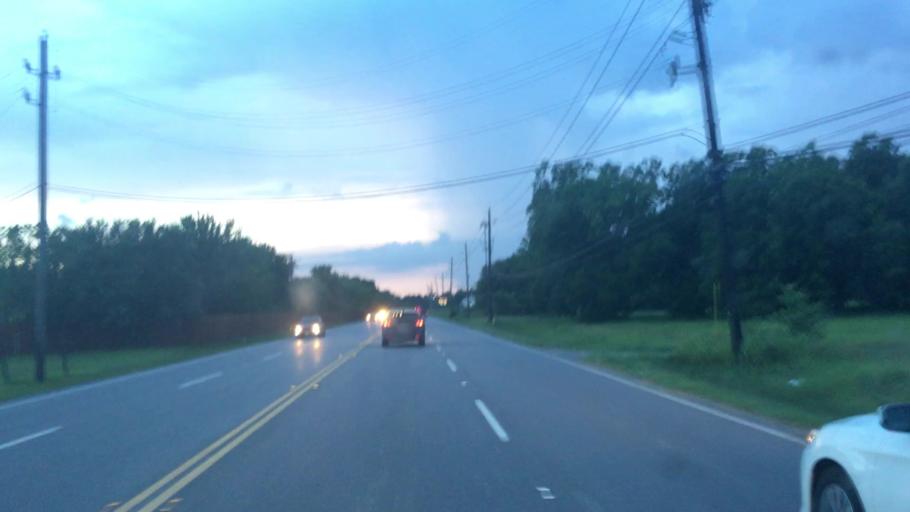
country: US
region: Texas
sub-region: Harris County
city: Humble
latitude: 29.9668
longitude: -95.2384
